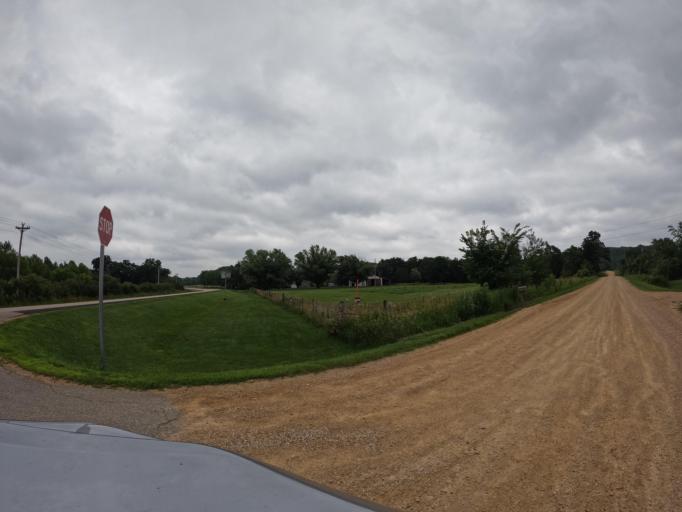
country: US
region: Illinois
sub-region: Carroll County
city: Savanna
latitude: 41.9966
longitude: -90.1849
